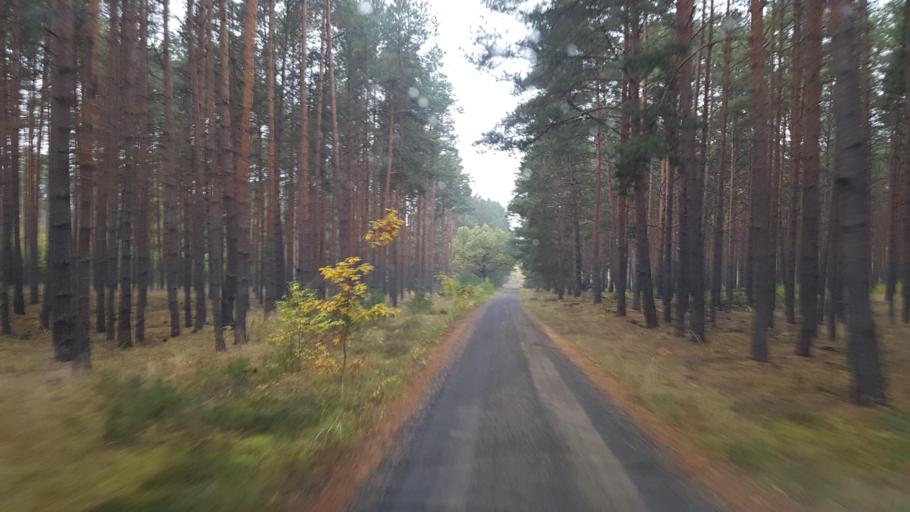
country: DE
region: Brandenburg
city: Schlieben
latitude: 51.7444
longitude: 13.3928
